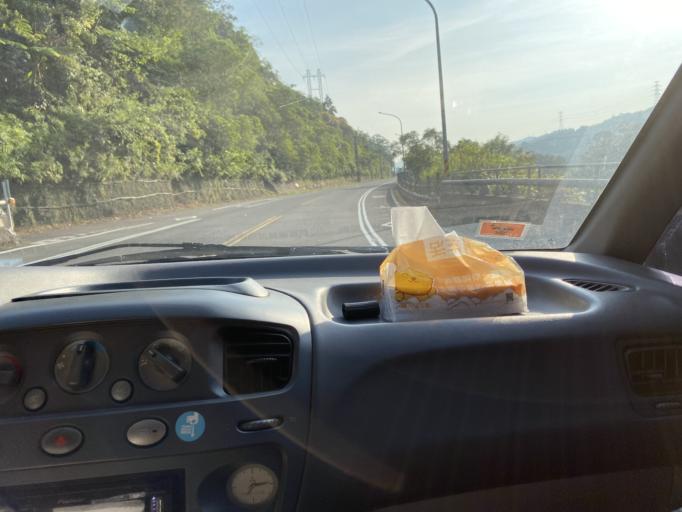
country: TW
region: Taiwan
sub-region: Keelung
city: Keelung
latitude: 25.0231
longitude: 121.8159
